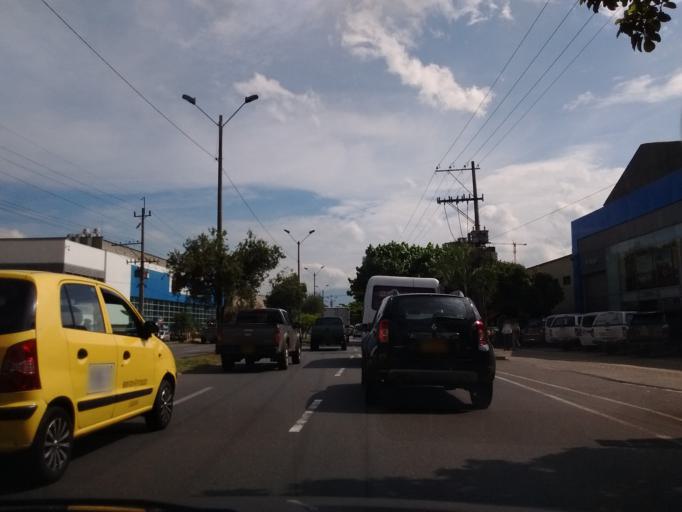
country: CO
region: Antioquia
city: Medellin
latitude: 6.2155
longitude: -75.5760
